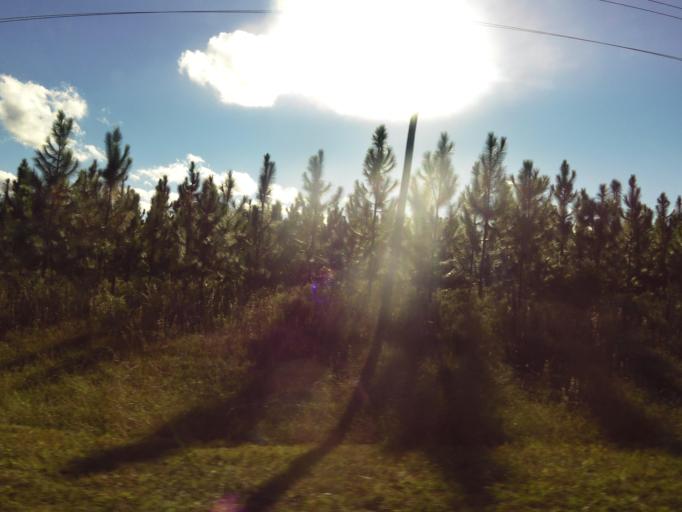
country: US
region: Florida
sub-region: Alachua County
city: Hawthorne
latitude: 29.5206
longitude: -82.1806
